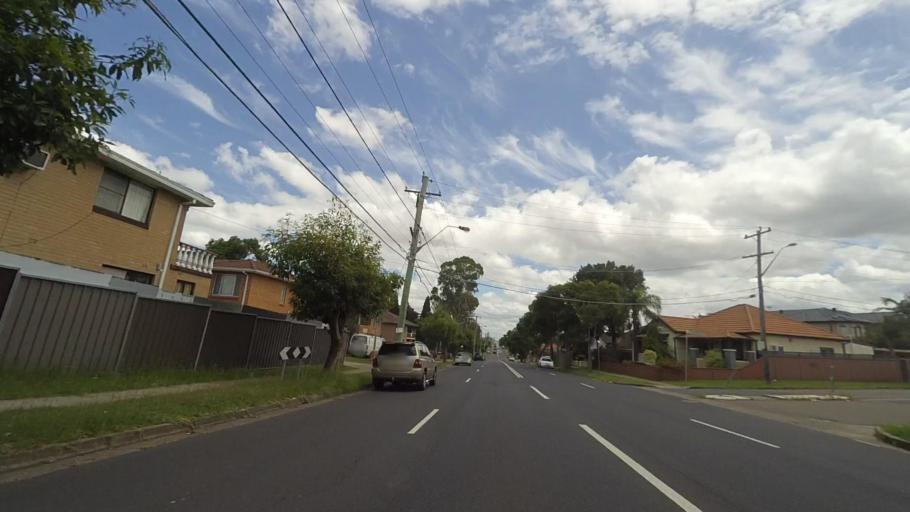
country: AU
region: New South Wales
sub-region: Fairfield
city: Fairfield Heights
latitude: -33.8678
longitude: 150.9486
